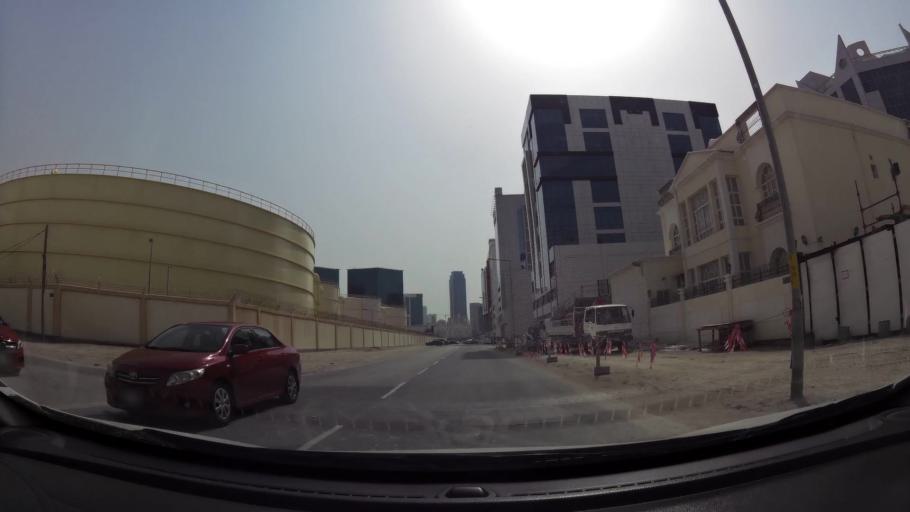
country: BH
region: Manama
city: Jidd Hafs
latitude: 26.2388
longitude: 50.5314
